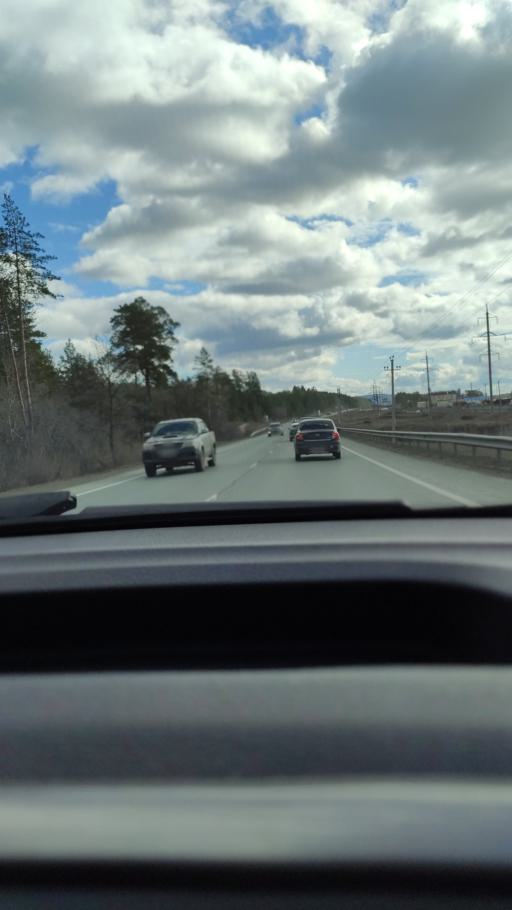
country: RU
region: Samara
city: Kurumoch
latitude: 53.4751
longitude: 50.0600
